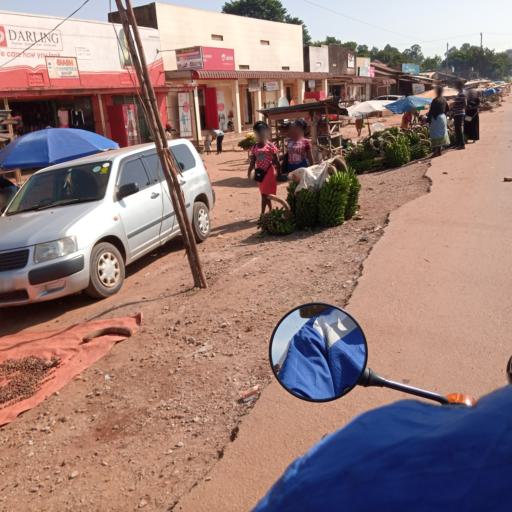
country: UG
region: Central Region
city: Masaka
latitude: -0.3743
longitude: 31.7147
